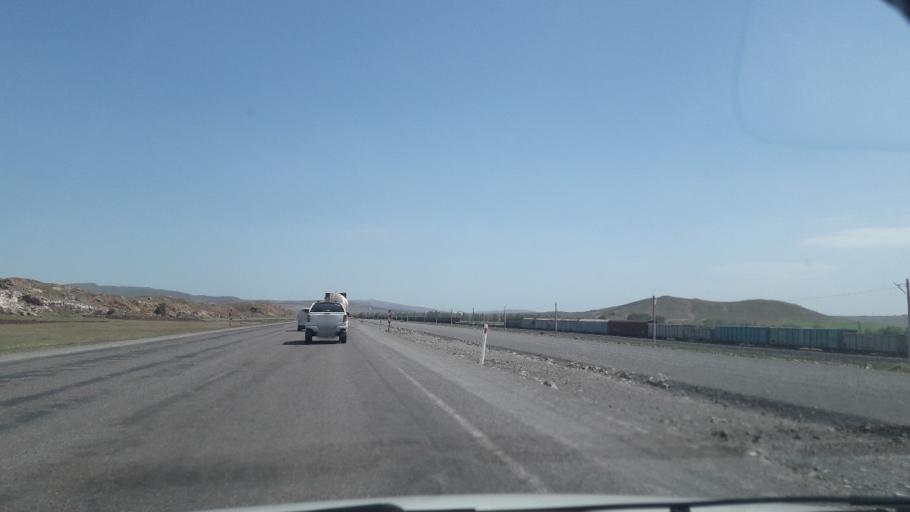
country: TR
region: Sivas
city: Ulas
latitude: 39.5359
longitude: 37.0188
